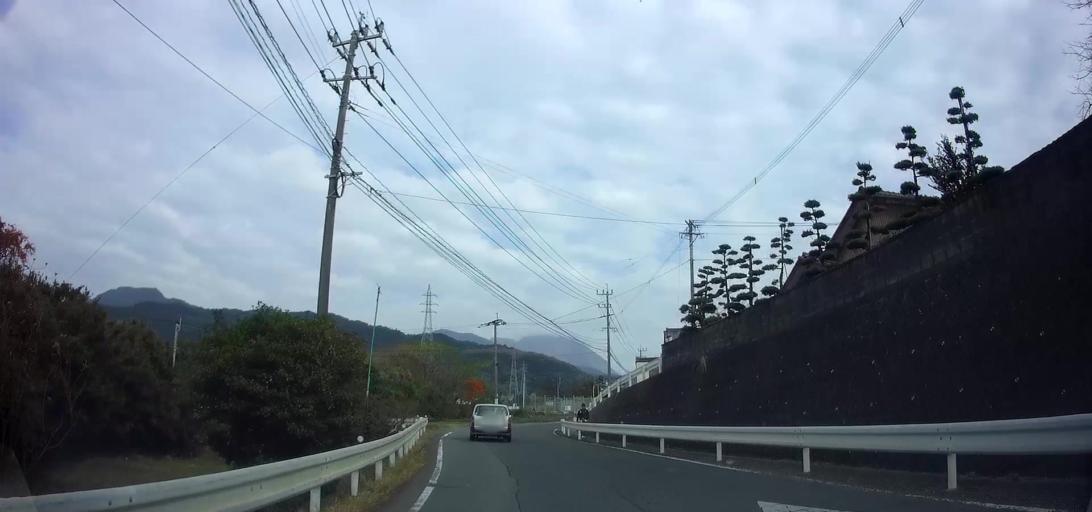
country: JP
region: Nagasaki
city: Shimabara
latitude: 32.6892
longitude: 130.2953
